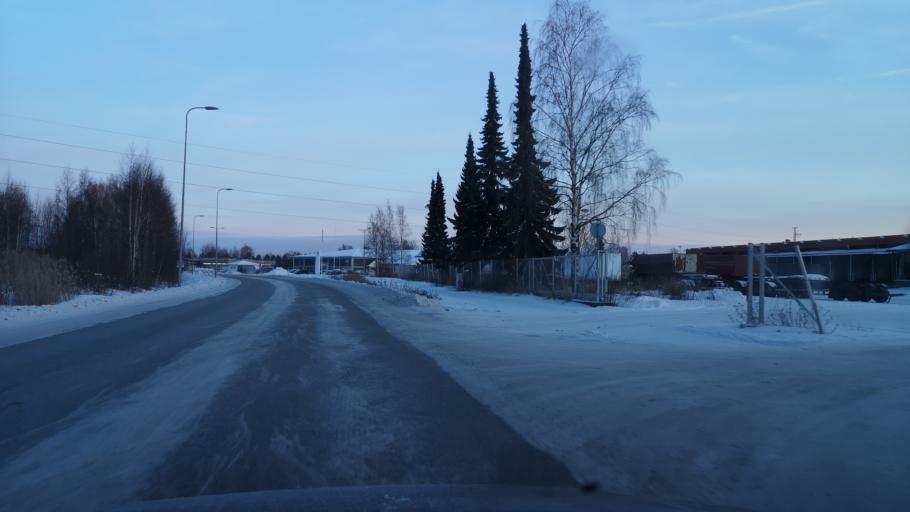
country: FI
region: Satakunta
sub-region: Pori
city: Pori
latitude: 61.4825
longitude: 21.8189
